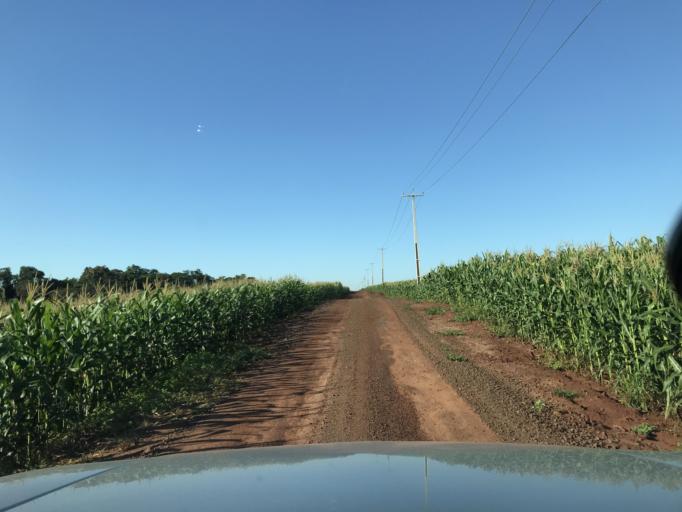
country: BR
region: Parana
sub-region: Palotina
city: Palotina
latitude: -24.2106
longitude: -53.7485
